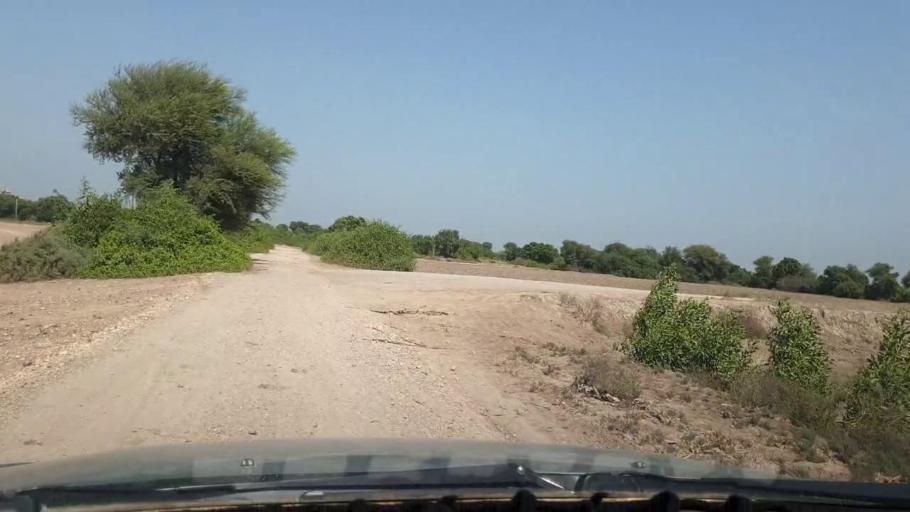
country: PK
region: Sindh
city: Tando Muhammad Khan
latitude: 25.1751
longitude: 68.6318
